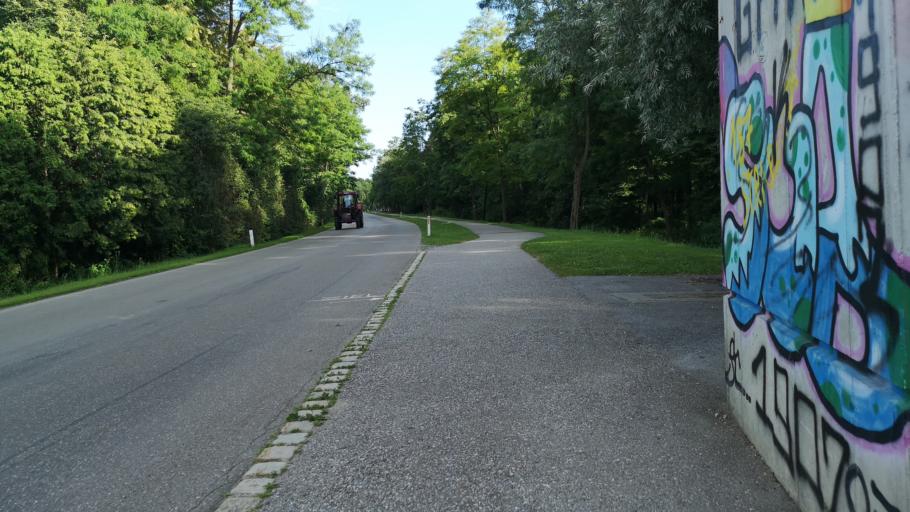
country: AT
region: Styria
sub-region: Politischer Bezirk Graz-Umgebung
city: Feldkirchen bei Graz
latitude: 47.0061
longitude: 15.4681
